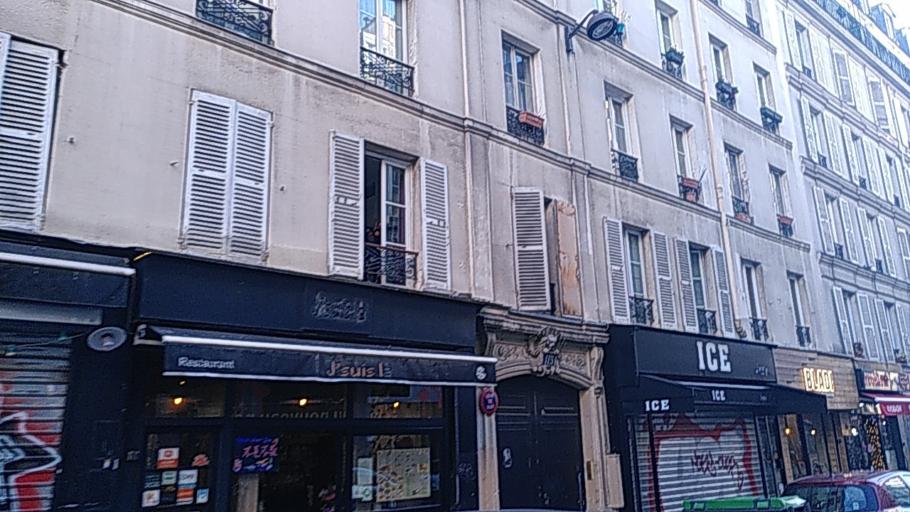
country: FR
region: Ile-de-France
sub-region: Paris
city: Paris
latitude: 48.8660
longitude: 2.3771
